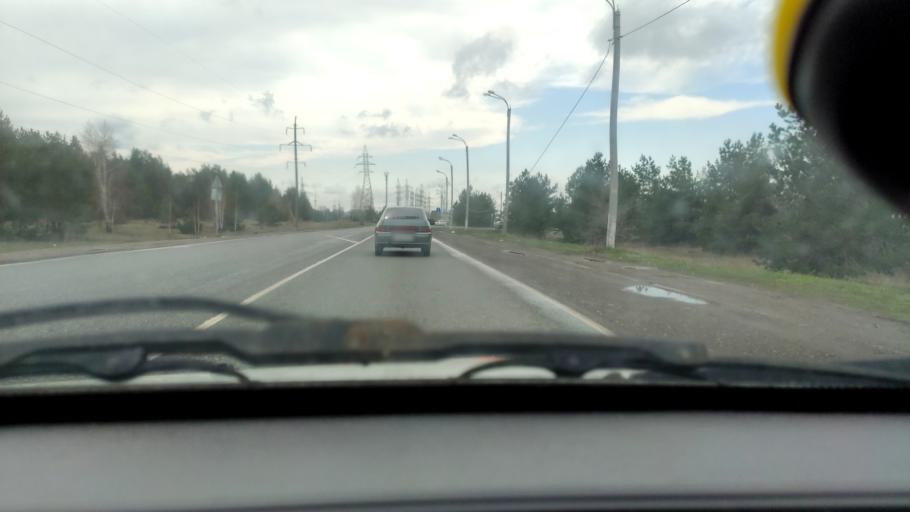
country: RU
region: Samara
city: Zhigulevsk
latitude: 53.5660
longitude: 49.5470
